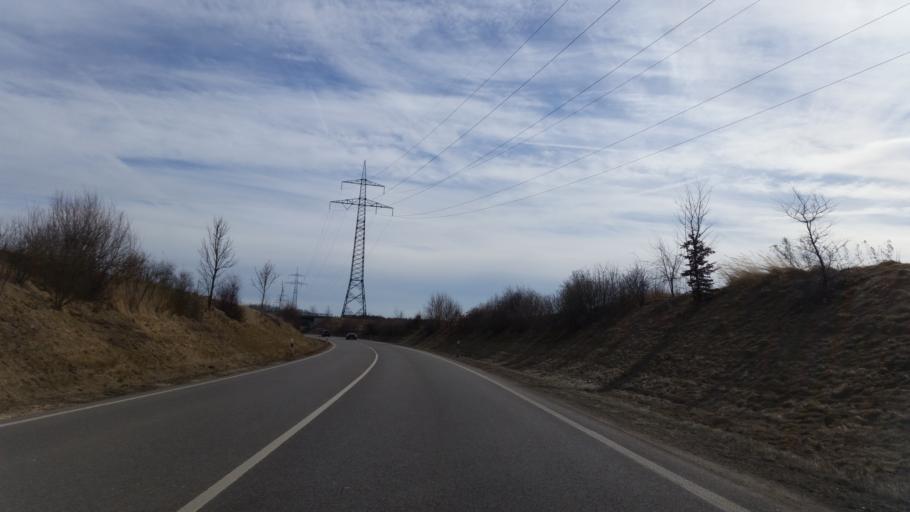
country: DE
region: Bavaria
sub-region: Upper Bavaria
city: Zorneding
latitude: 48.0775
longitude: 11.8115
